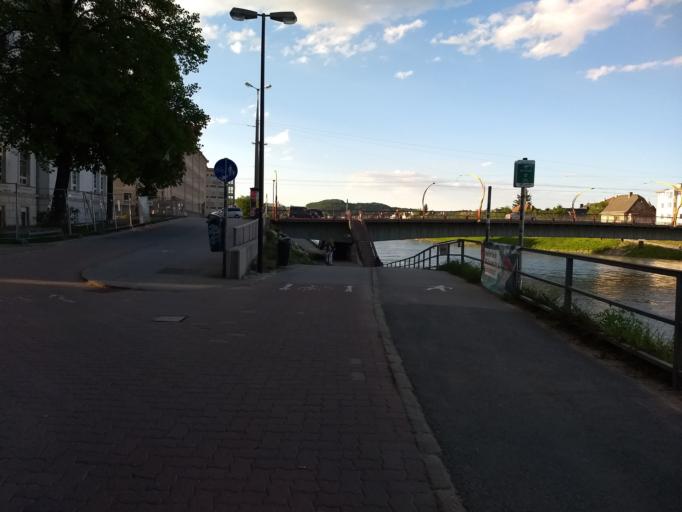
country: AT
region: Salzburg
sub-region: Salzburg Stadt
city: Salzburg
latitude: 47.8104
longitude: 13.0358
